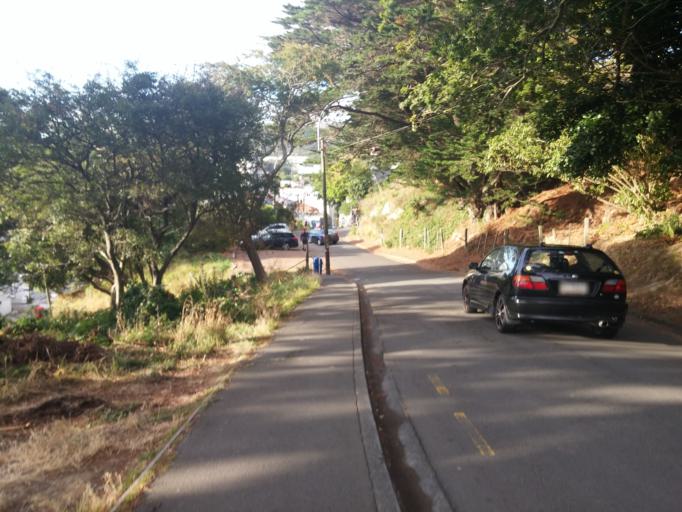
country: NZ
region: Wellington
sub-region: Wellington City
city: Wellington
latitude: -41.2928
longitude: 174.7694
